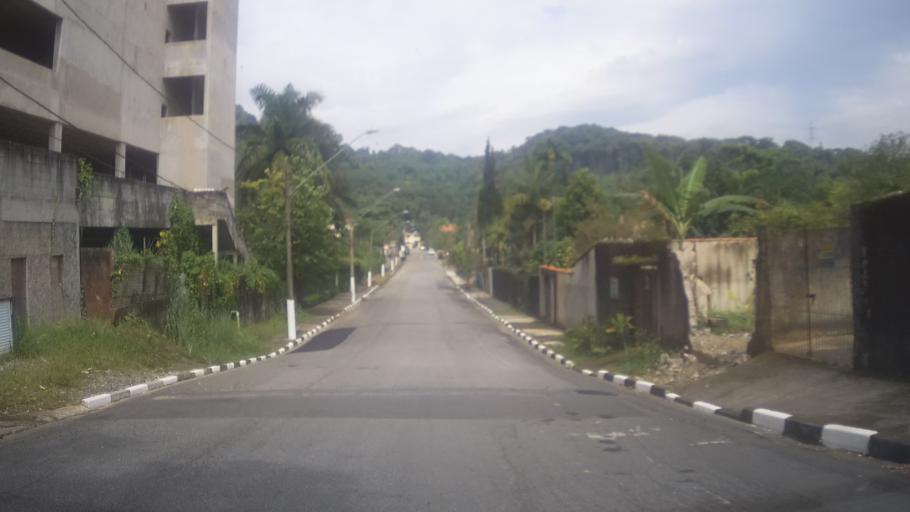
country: BR
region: Sao Paulo
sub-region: Santos
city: Santos
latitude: -23.9483
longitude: -46.3562
